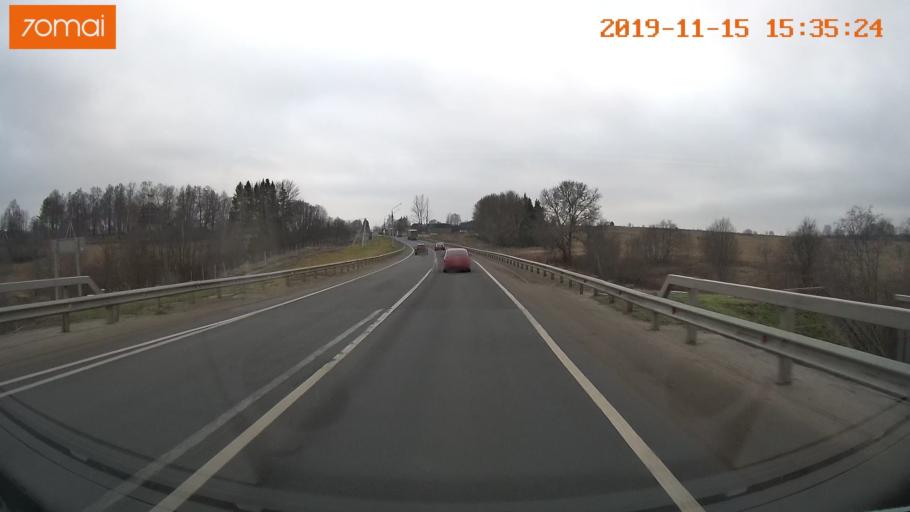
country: RU
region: Jaroslavl
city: Danilov
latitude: 58.0595
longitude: 40.0876
